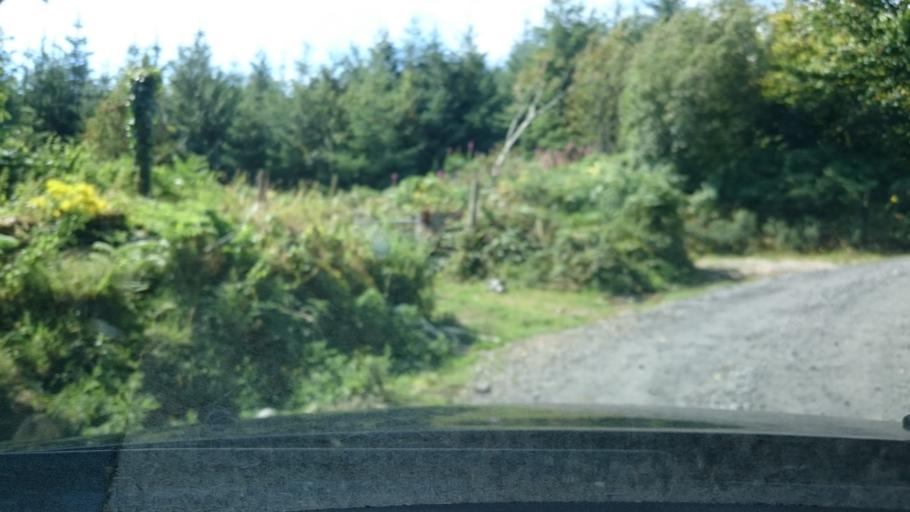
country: IE
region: Leinster
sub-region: Kilkenny
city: Graiguenamanagh
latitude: 52.5216
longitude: -6.9643
